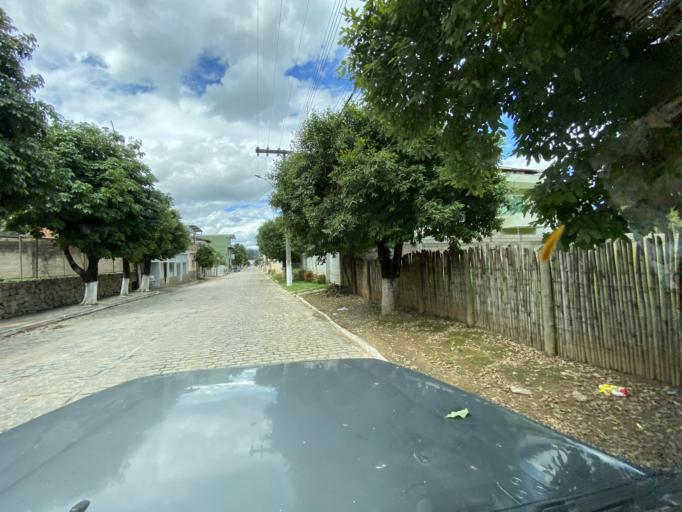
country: BR
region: Espirito Santo
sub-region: Jeronimo Monteiro
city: Jeronimo Monteiro
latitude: -20.7864
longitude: -41.3903
